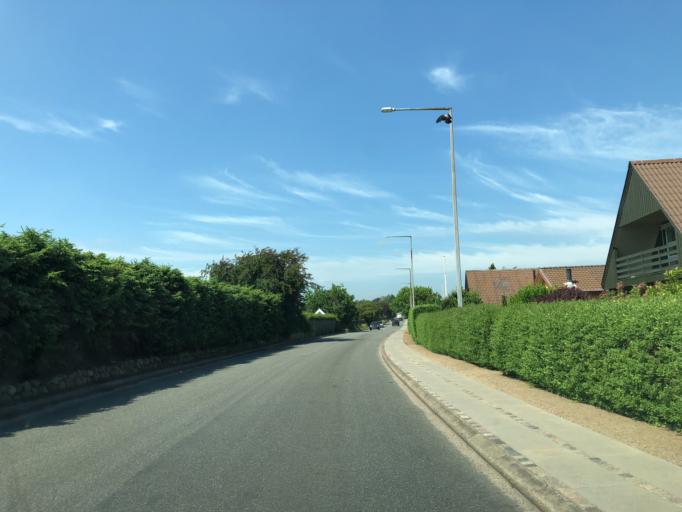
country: DK
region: South Denmark
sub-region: Kolding Kommune
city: Kolding
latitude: 55.5235
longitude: 9.4718
